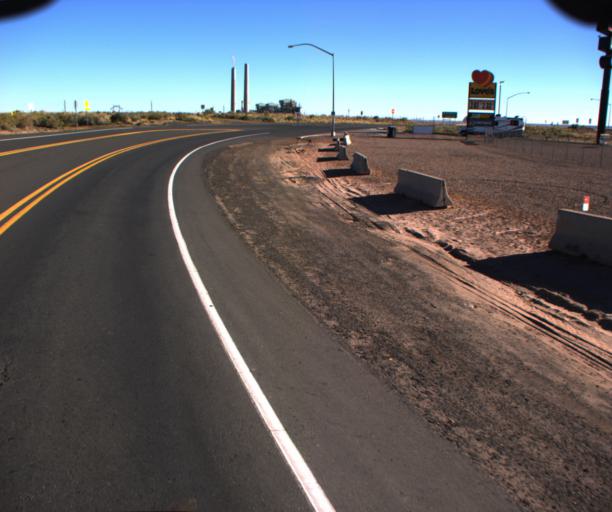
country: US
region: Arizona
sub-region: Navajo County
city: Joseph City
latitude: 34.9551
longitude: -110.3104
